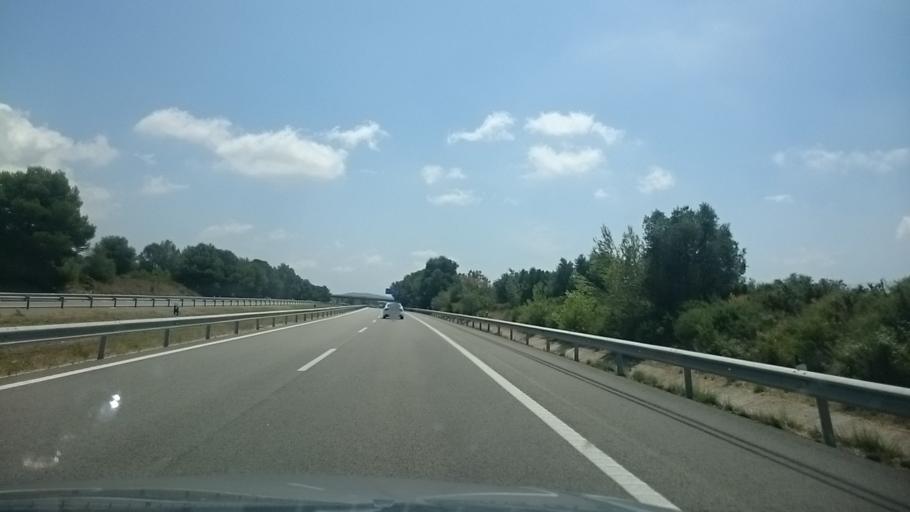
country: ES
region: Catalonia
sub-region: Provincia de Tarragona
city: Alio
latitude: 41.3095
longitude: 1.3395
